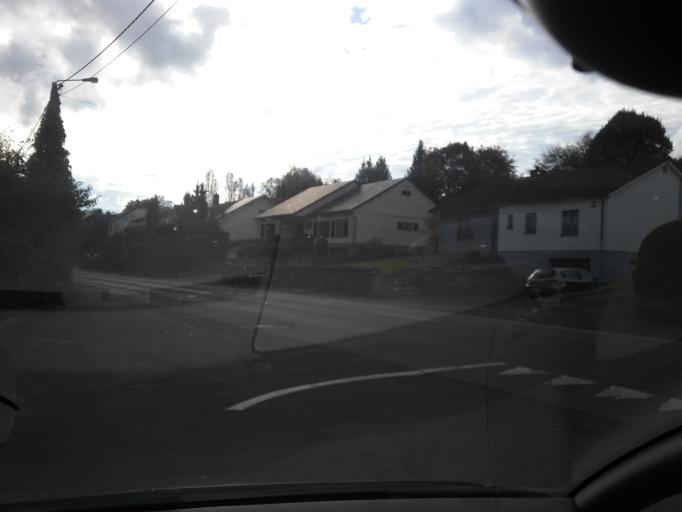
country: BE
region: Wallonia
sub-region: Province du Luxembourg
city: Arlon
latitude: 49.7021
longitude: 5.8268
